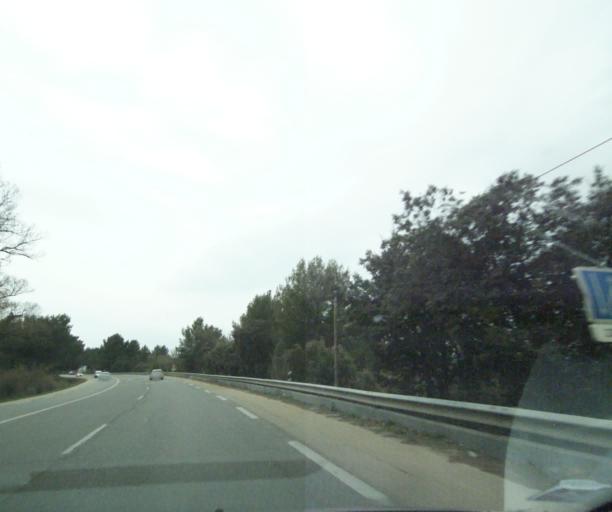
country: FR
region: Provence-Alpes-Cote d'Azur
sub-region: Departement des Bouches-du-Rhone
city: Meyrargues
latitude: 43.6383
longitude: 5.5174
